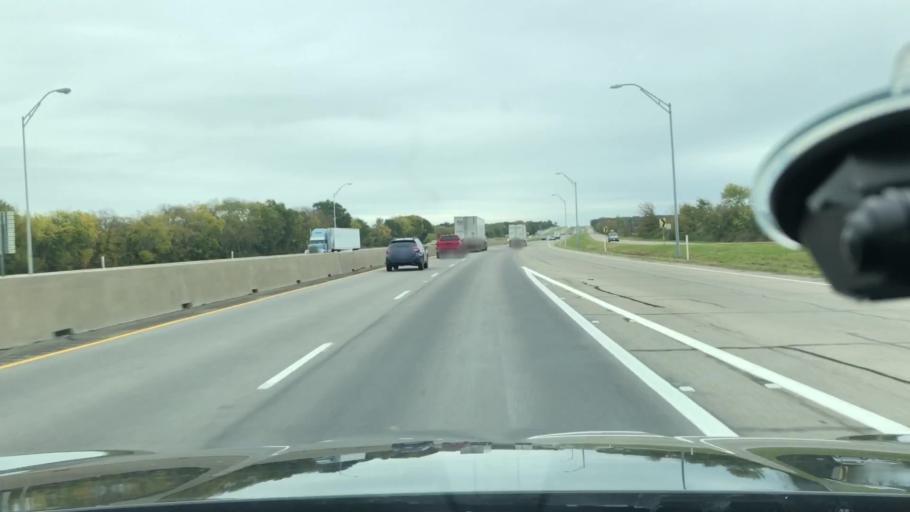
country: US
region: Texas
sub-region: Hopkins County
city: Sulphur Springs
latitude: 33.1446
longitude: -95.5610
